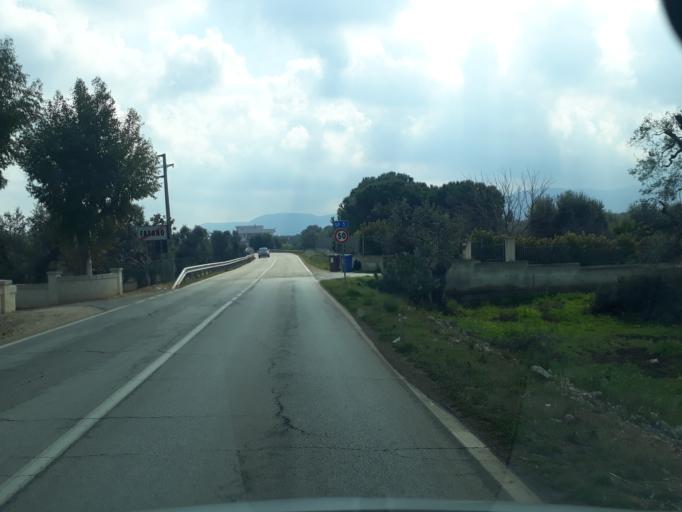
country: IT
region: Apulia
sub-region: Provincia di Brindisi
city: Fasano
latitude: 40.8247
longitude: 17.3711
